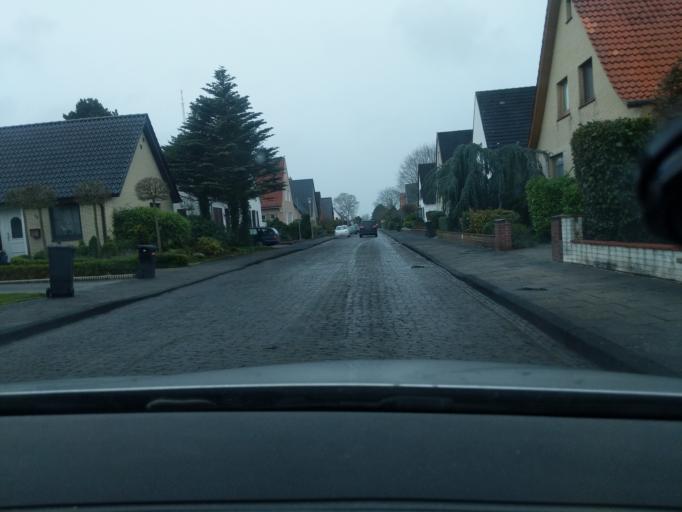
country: DE
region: Lower Saxony
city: Cuxhaven
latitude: 53.8581
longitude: 8.6905
